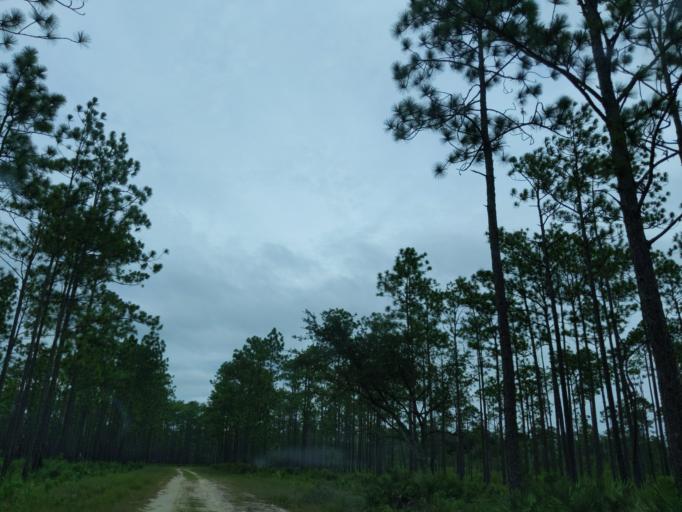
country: US
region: Florida
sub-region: Gadsden County
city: Midway
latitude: 30.3605
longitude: -84.4865
